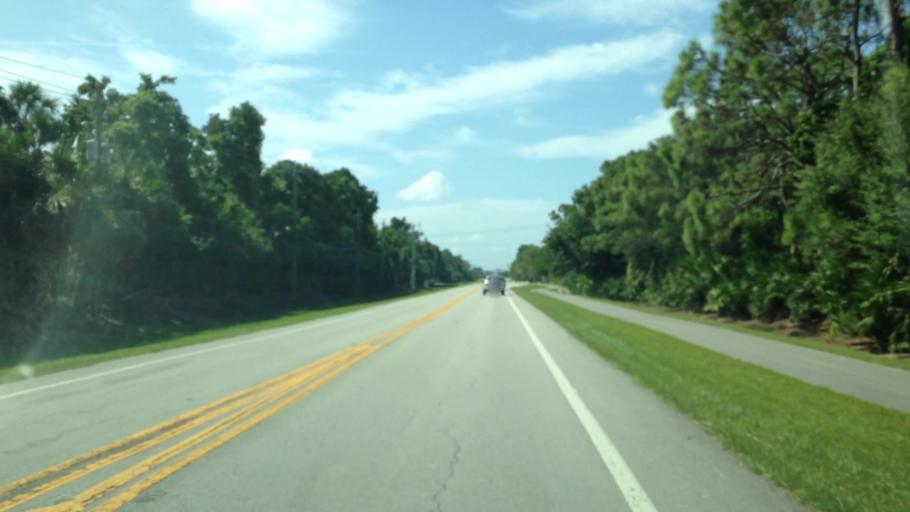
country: US
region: Florida
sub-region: Collier County
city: Naples Park
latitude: 26.3084
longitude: -81.8188
